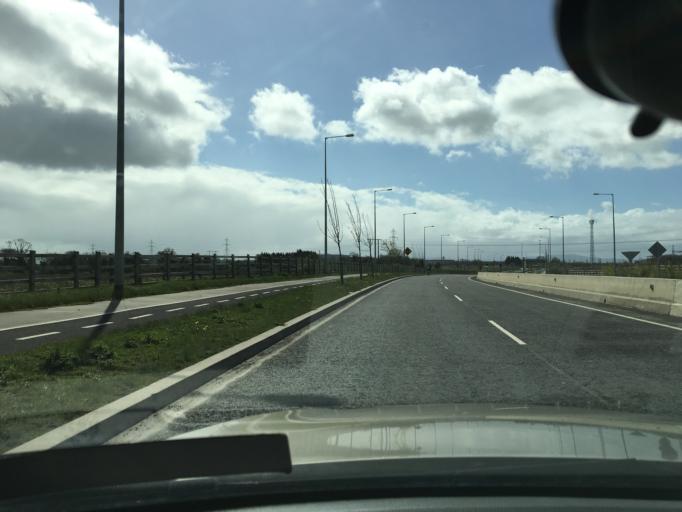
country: IE
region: Leinster
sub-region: Fingal County
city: Blanchardstown
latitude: 53.4221
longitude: -6.3620
